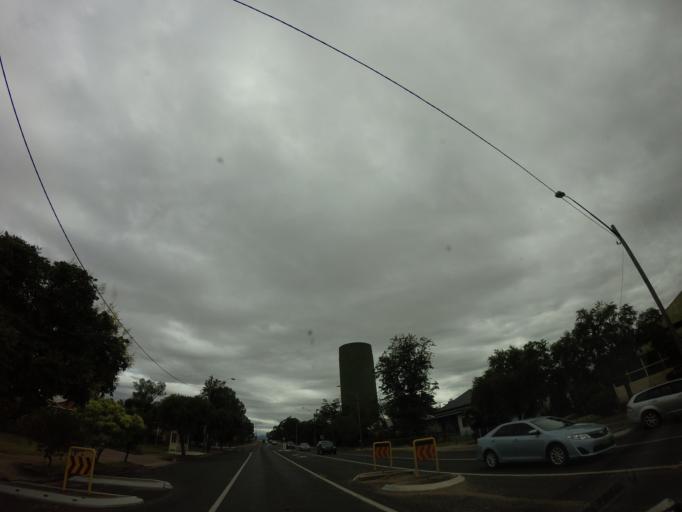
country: AU
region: New South Wales
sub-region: Narrabri
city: Narrabri
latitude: -30.3282
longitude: 149.7784
